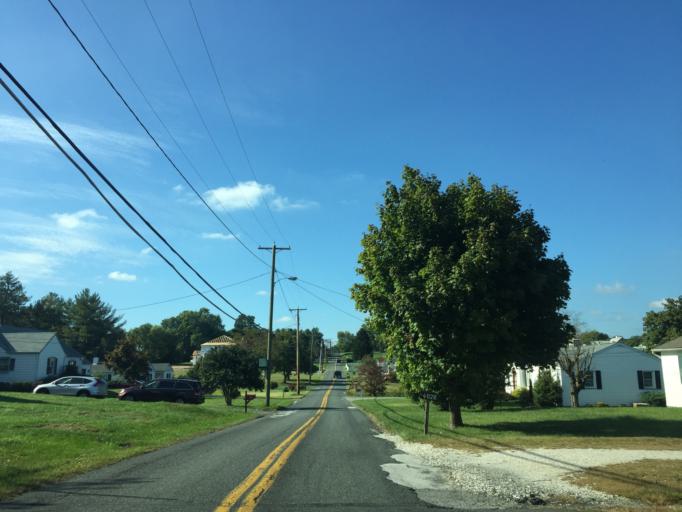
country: US
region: Maryland
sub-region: Baltimore County
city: Perry Hall
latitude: 39.4184
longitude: -76.4581
